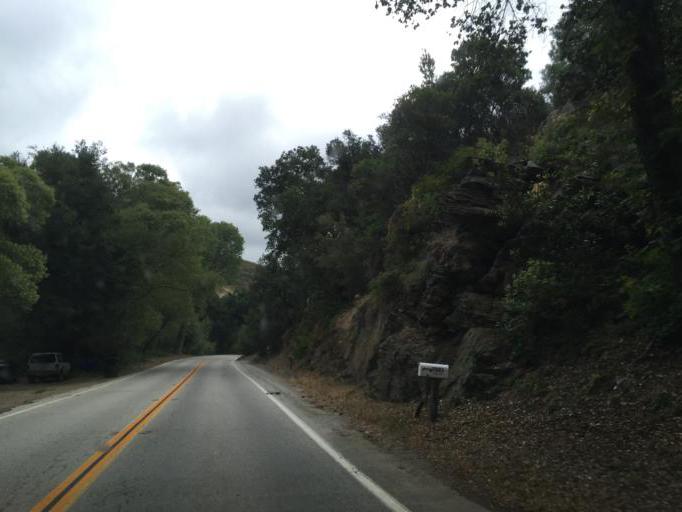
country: US
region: California
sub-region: Los Angeles County
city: Green Valley
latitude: 34.5536
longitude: -118.4211
